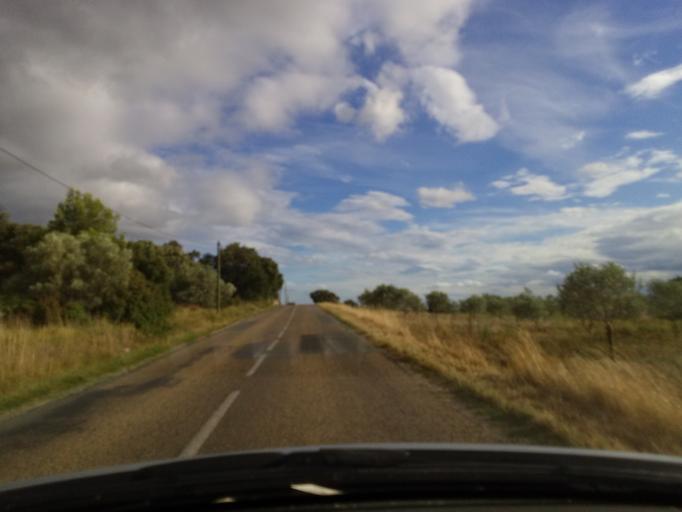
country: FR
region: Languedoc-Roussillon
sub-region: Departement de l'Herault
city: Saint-Jean-de-Fos
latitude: 43.6873
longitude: 3.5406
